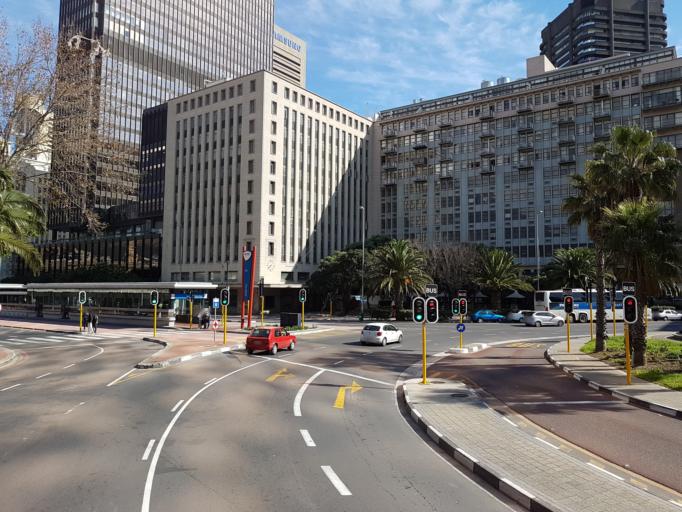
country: ZA
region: Western Cape
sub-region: City of Cape Town
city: Cape Town
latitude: -33.9202
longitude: 18.4257
